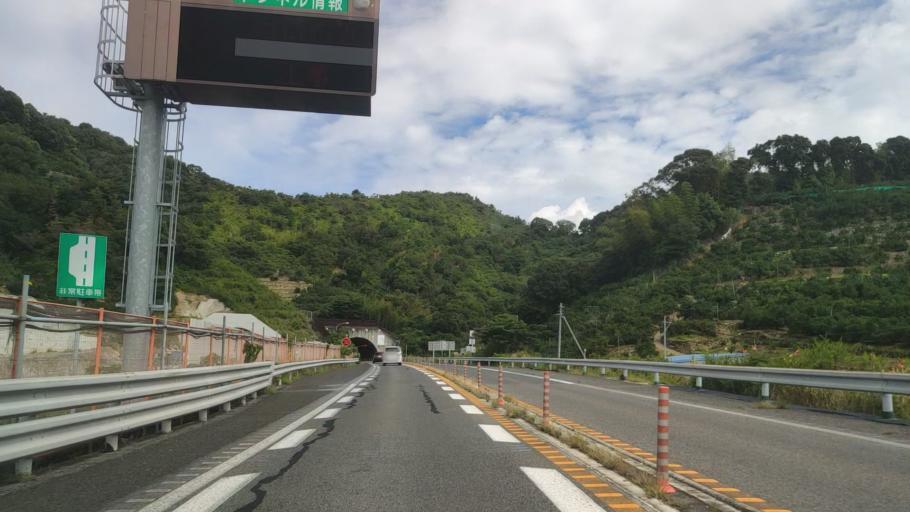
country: JP
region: Wakayama
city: Kainan
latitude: 34.0208
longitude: 135.1973
